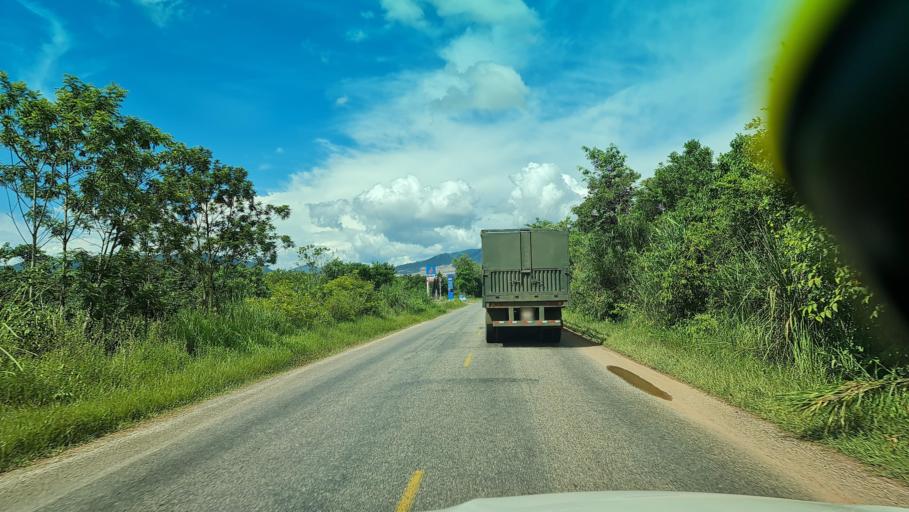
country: LA
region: Bolikhamxai
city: Pakkading
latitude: 18.2917
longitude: 104.0813
